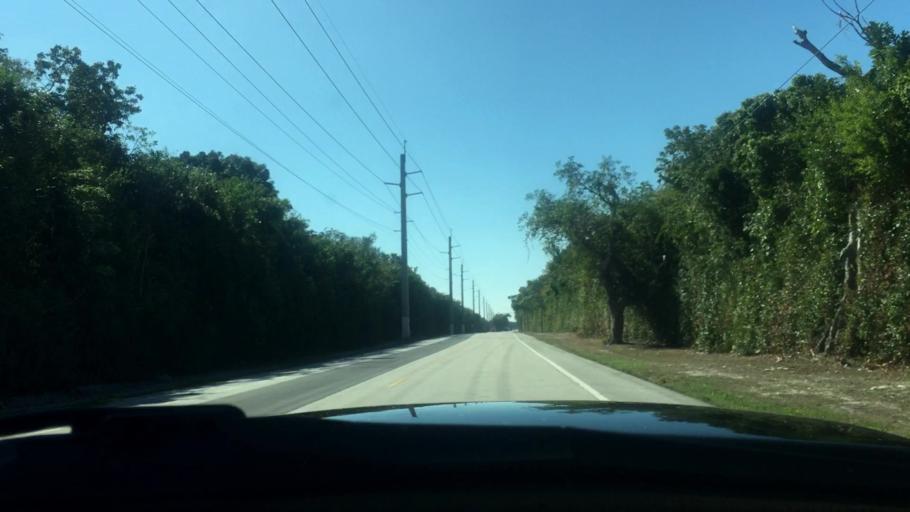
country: US
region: Florida
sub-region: Monroe County
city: North Key Largo
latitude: 25.2162
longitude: -80.3375
